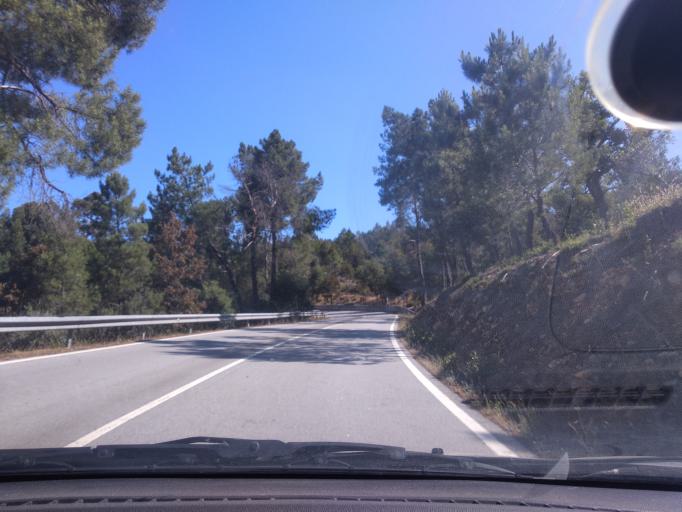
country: PT
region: Portalegre
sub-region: Nisa
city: Nisa
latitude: 39.6040
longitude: -7.6607
